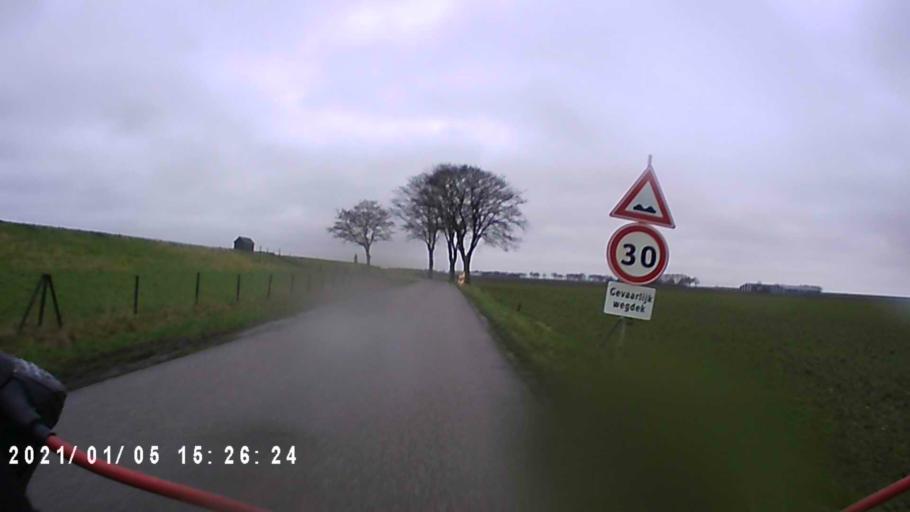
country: DE
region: Lower Saxony
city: Bunde
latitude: 53.2230
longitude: 7.1982
